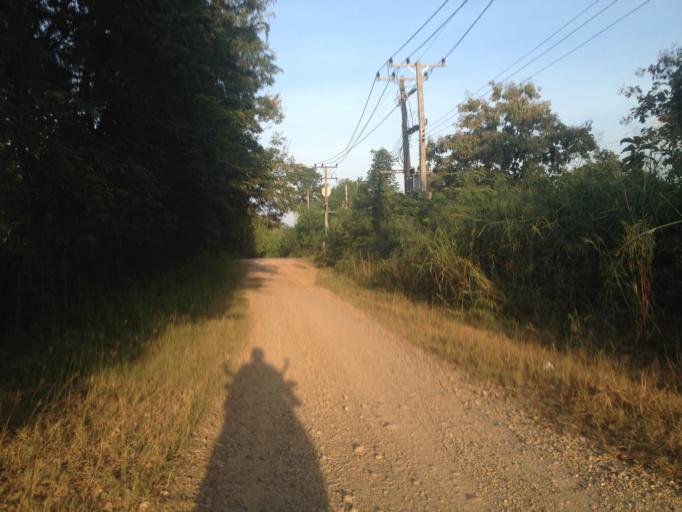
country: TH
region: Chiang Mai
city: Chiang Mai
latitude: 18.7650
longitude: 98.9339
